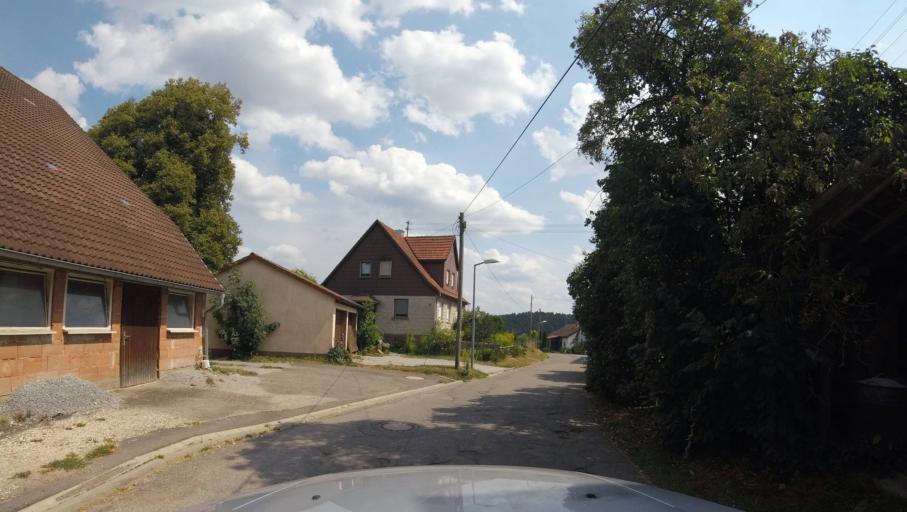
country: DE
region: Baden-Wuerttemberg
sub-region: Regierungsbezirk Stuttgart
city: Alfdorf
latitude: 48.8676
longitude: 9.7304
